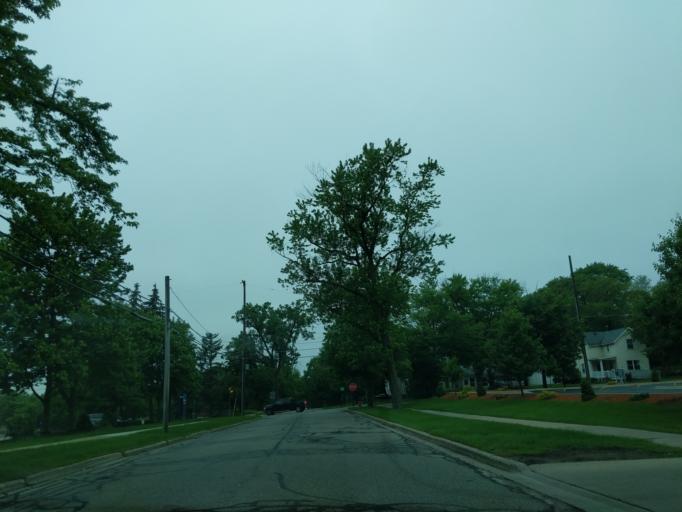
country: US
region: Michigan
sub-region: Jackson County
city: Jackson
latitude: 42.2523
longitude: -84.3948
